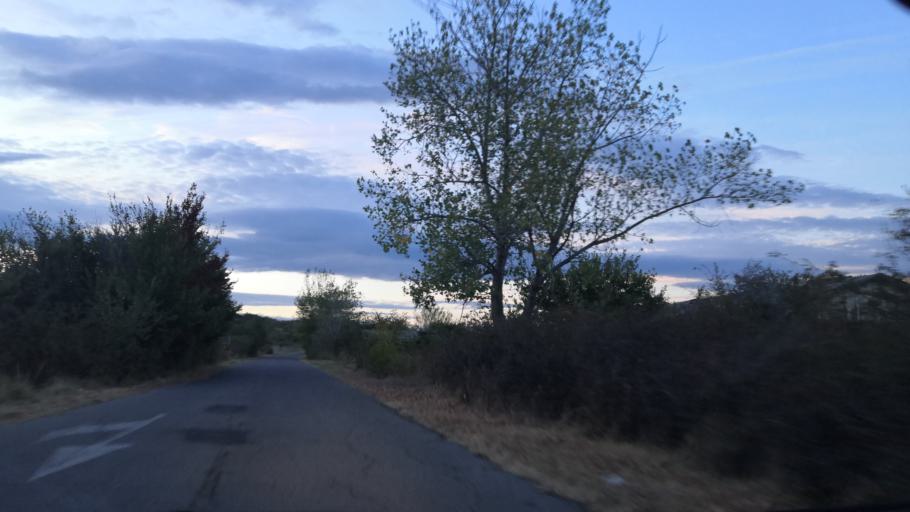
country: RO
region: Mehedinti
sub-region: Comuna Gogosu
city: Balta Verde
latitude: 44.2974
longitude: 22.5546
